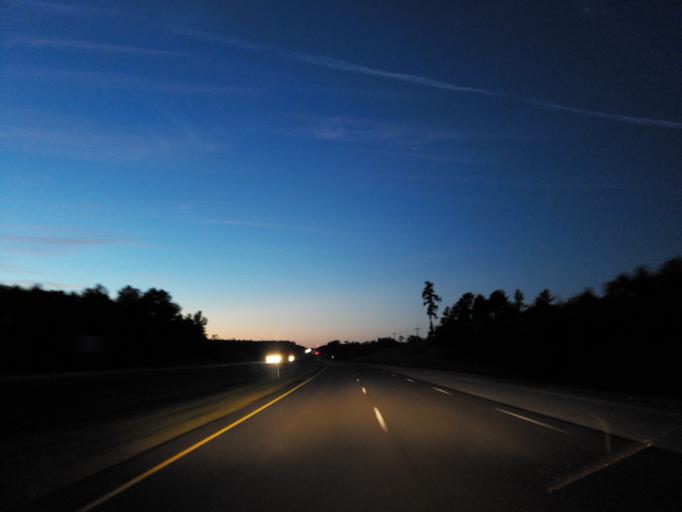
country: US
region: Mississippi
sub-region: Clarke County
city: Quitman
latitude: 32.0646
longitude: -88.6807
